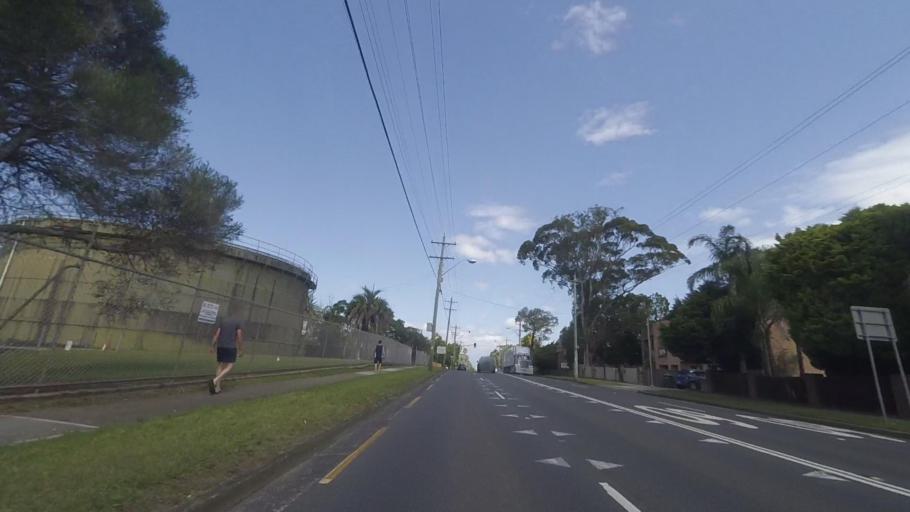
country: AU
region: New South Wales
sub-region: Parramatta
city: Carlingford
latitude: -33.7810
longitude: 151.0542
